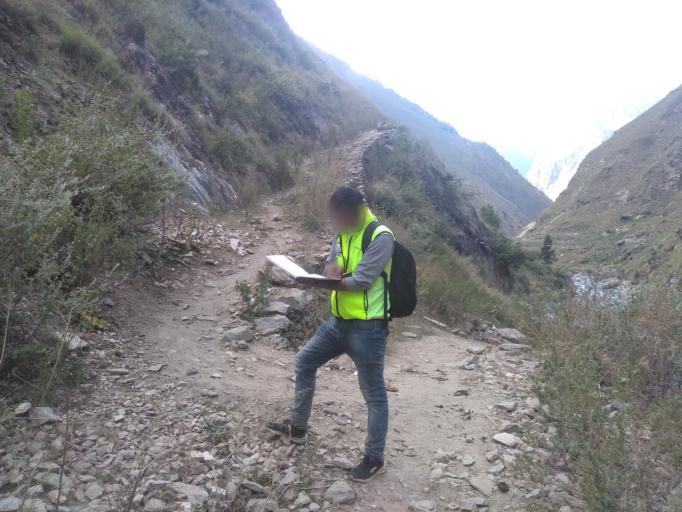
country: NP
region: Western Region
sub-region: Dhawalagiri Zone
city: Jomsom
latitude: 28.8928
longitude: 82.9836
